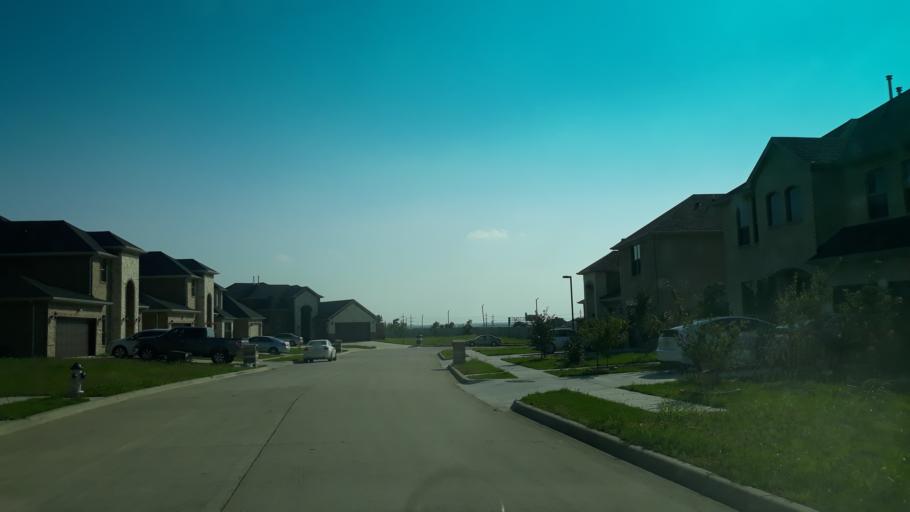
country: US
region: Texas
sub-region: Dallas County
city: Irving
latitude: 32.8626
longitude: -97.0048
